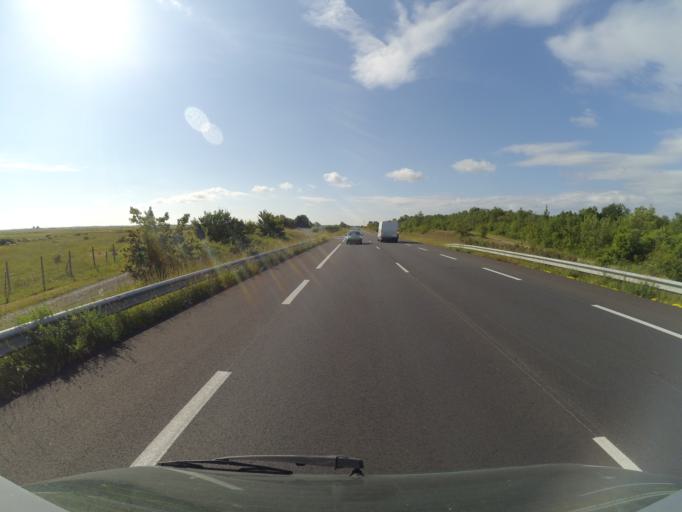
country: FR
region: Poitou-Charentes
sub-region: Departement de la Charente-Maritime
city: Saint-Agnant
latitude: 45.8448
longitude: -0.9510
